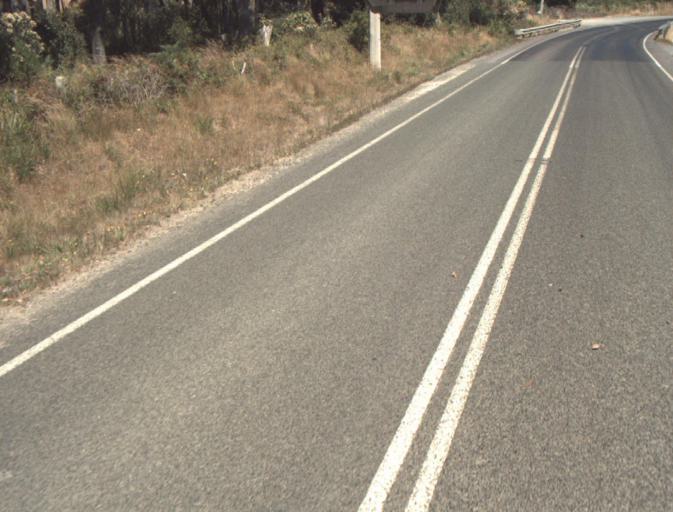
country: AU
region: Tasmania
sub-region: Launceston
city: Newstead
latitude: -41.3238
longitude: 147.3609
